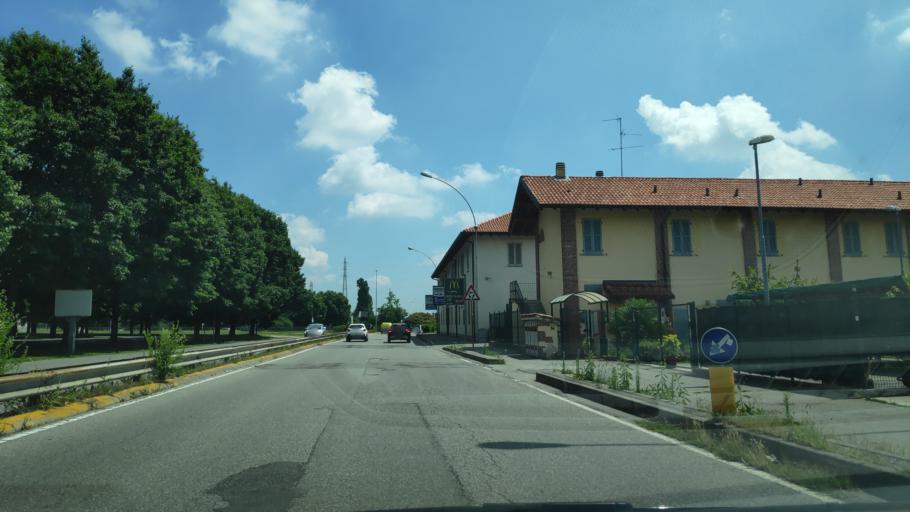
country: IT
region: Lombardy
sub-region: Provincia di Monza e Brianza
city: Villasanta
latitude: 45.5812
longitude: 9.3076
